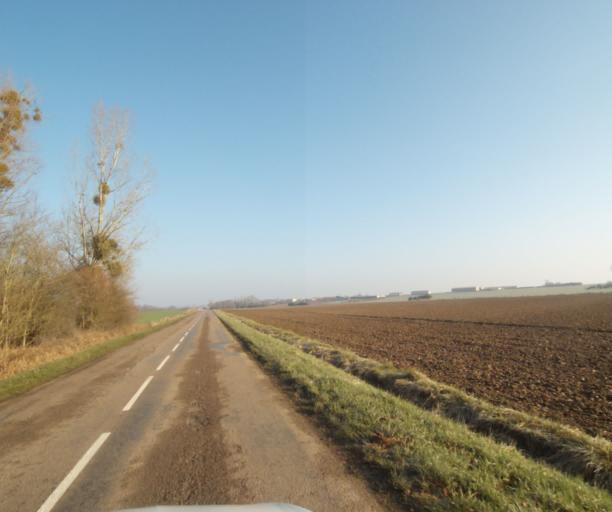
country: FR
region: Champagne-Ardenne
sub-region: Departement de la Haute-Marne
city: Montier-en-Der
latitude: 48.4443
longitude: 4.7596
